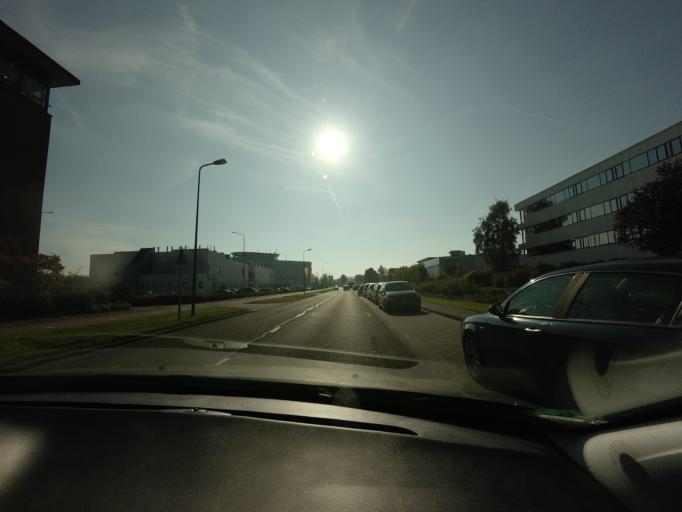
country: NL
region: Utrecht
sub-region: Gemeente Woerden
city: Woerden
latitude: 52.0776
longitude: 4.8953
